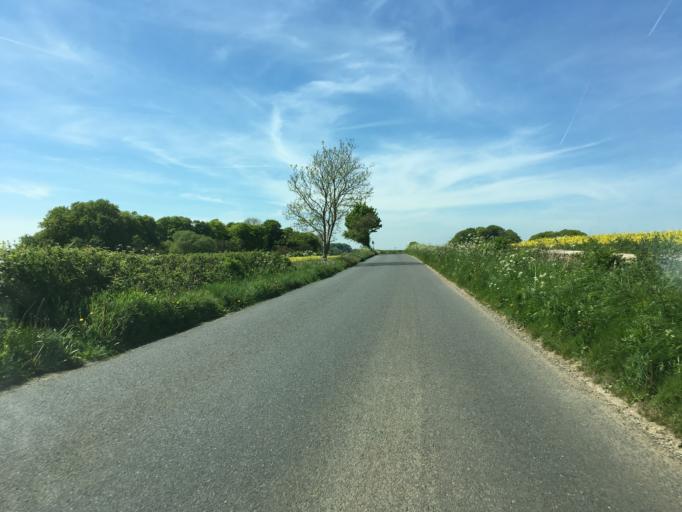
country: GB
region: England
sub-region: Gloucestershire
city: Coates
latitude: 51.7200
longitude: -2.0662
